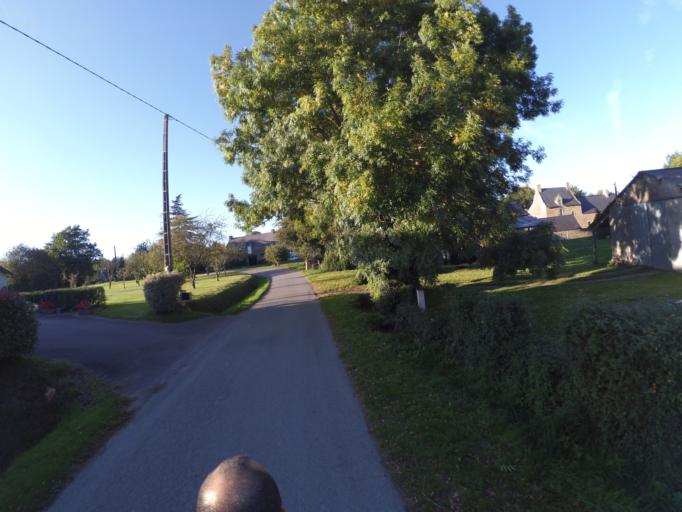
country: FR
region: Brittany
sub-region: Departement du Morbihan
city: Peillac
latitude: 47.7216
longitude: -2.1963
